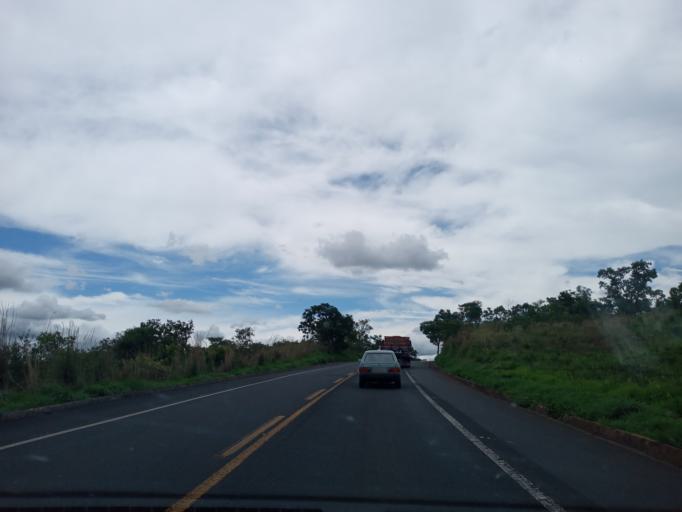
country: BR
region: Minas Gerais
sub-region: Uberlandia
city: Uberlandia
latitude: -19.1683
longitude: -47.9006
